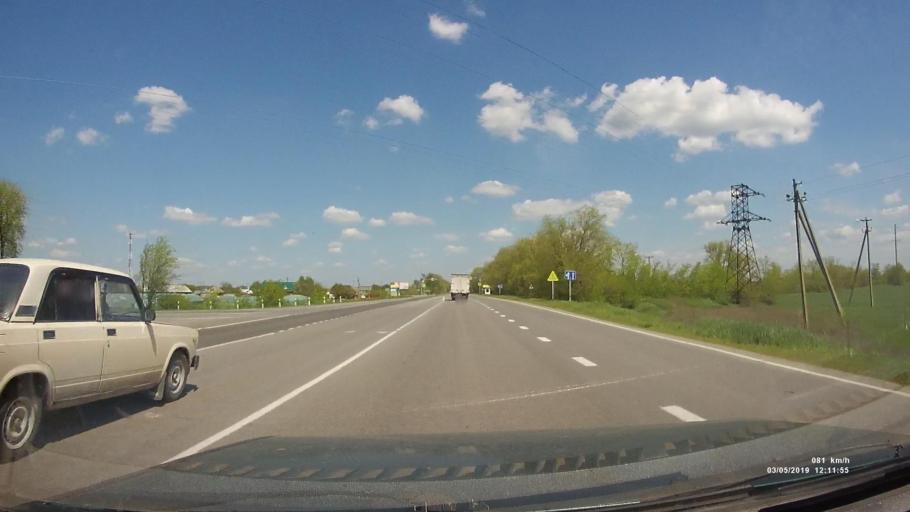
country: RU
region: Rostov
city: Bagayevskaya
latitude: 47.3156
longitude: 40.5422
